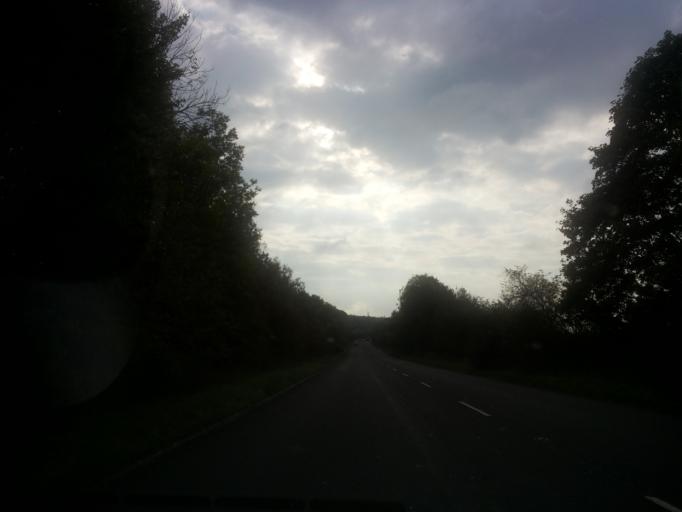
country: GB
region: England
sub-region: Buckinghamshire
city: Great Missenden
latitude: 51.7095
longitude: -0.7093
